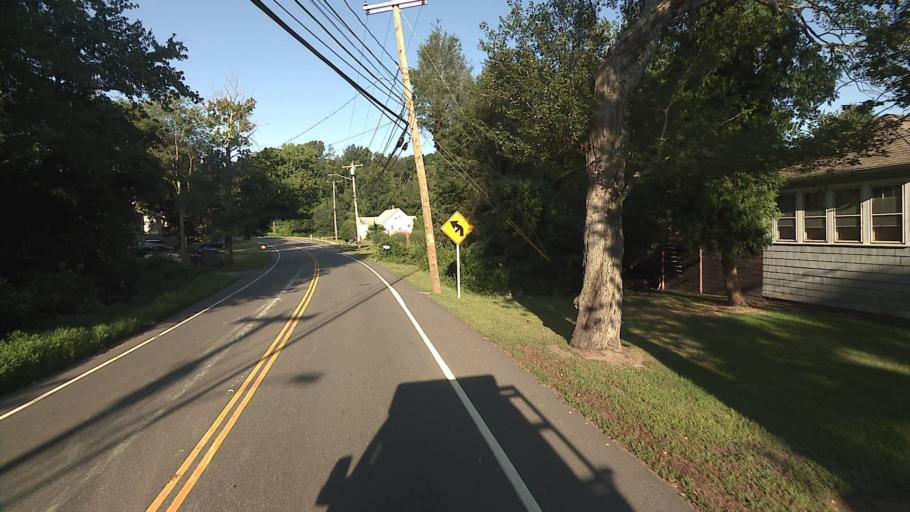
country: US
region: Connecticut
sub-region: New London County
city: Noank
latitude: 41.3535
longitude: -71.9938
